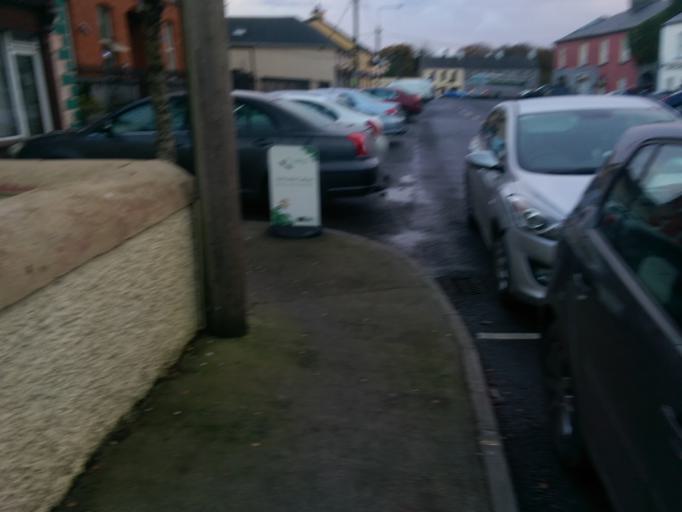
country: IE
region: Connaught
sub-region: County Galway
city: Loughrea
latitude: 53.4711
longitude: -8.4997
